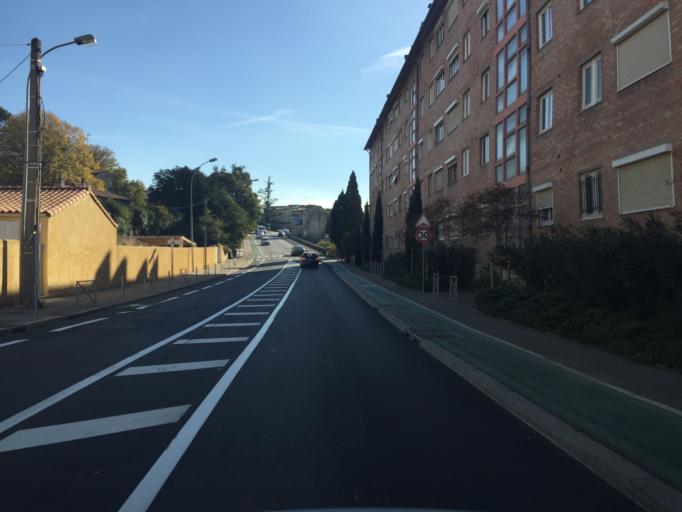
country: FR
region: Provence-Alpes-Cote d'Azur
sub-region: Departement des Bouches-du-Rhone
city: Salon-de-Provence
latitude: 43.6377
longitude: 5.1025
